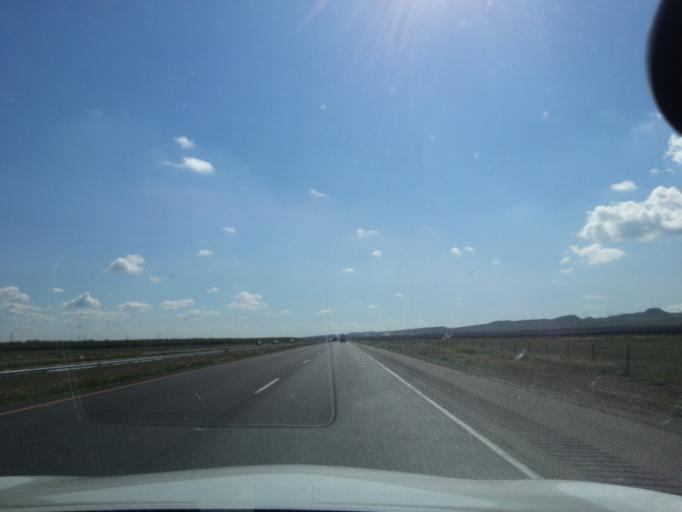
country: US
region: California
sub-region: Fresno County
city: Coalinga
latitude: 36.3680
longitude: -120.3338
